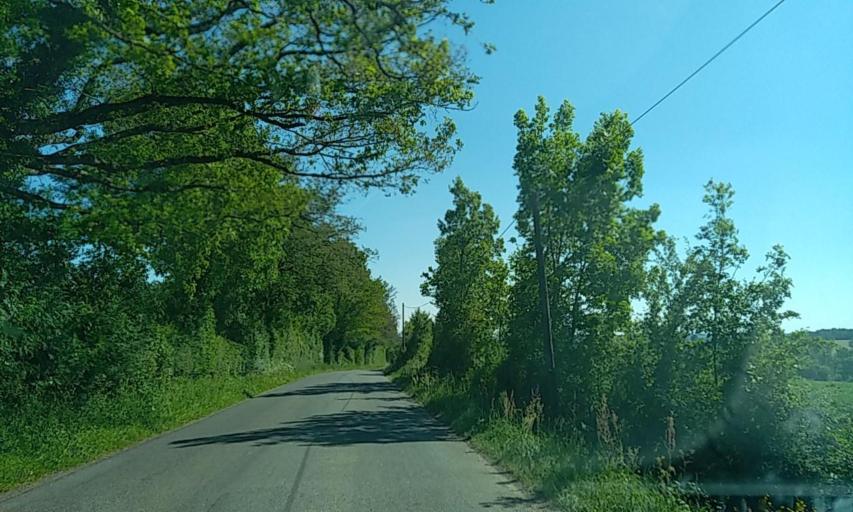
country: FR
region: Poitou-Charentes
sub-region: Departement des Deux-Sevres
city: Boisme
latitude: 46.7915
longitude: -0.4517
